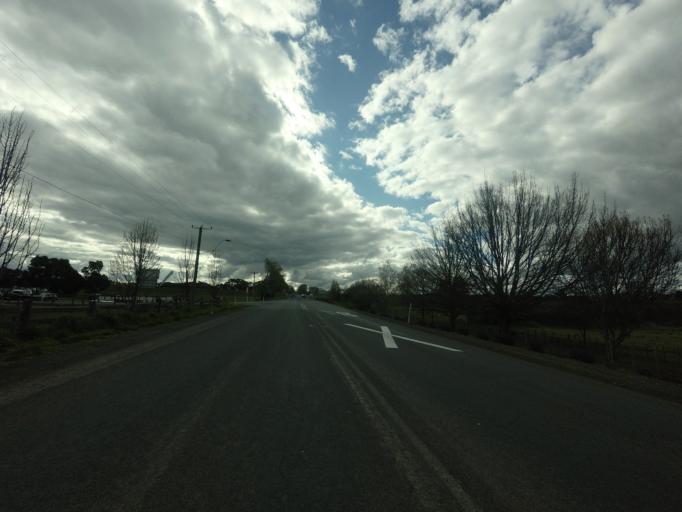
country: AU
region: Tasmania
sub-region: Northern Midlands
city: Longford
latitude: -41.5865
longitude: 147.1179
